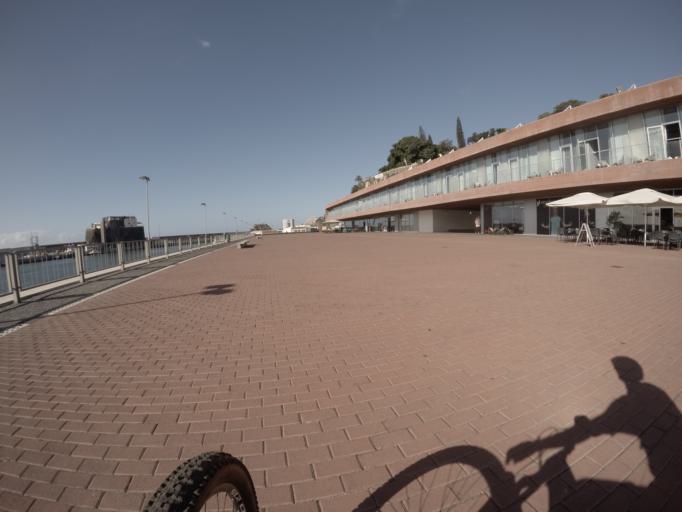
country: PT
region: Madeira
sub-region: Funchal
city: Funchal
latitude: 32.6438
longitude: -16.9139
